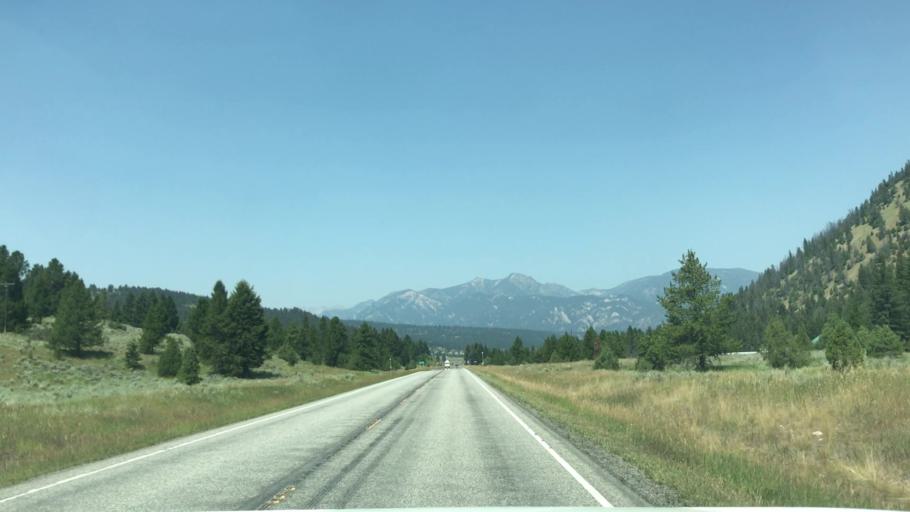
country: US
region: Montana
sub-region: Gallatin County
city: Big Sky
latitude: 45.2046
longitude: -111.2419
